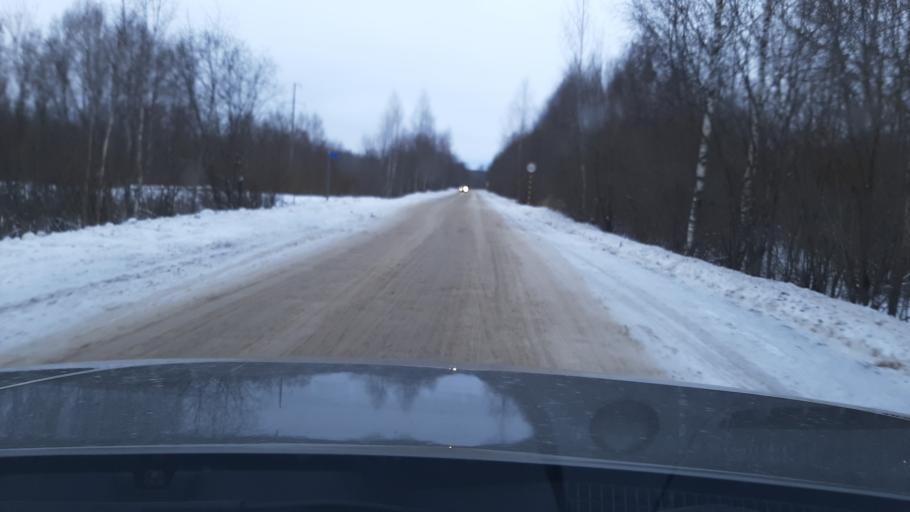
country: RU
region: Kostroma
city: Volgorechensk
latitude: 57.4430
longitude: 41.1293
